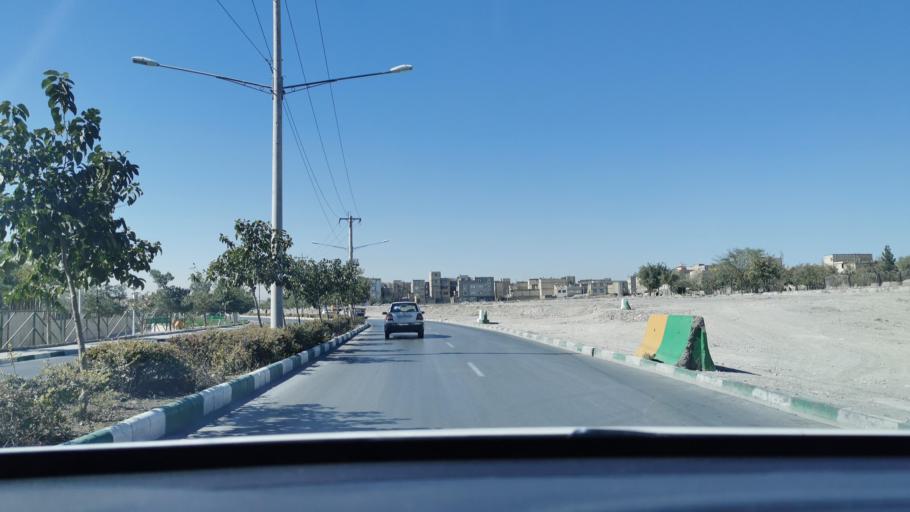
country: IR
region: Razavi Khorasan
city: Mashhad
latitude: 36.3358
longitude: 59.6141
